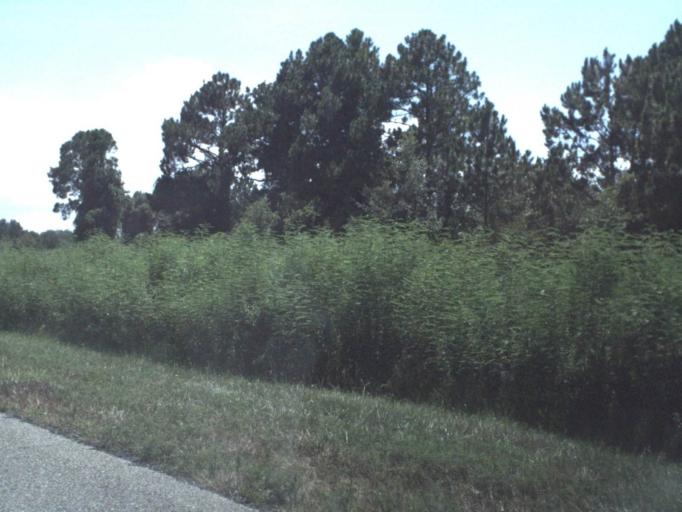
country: US
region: Florida
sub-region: Alachua County
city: Hawthorne
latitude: 29.5253
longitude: -82.1028
